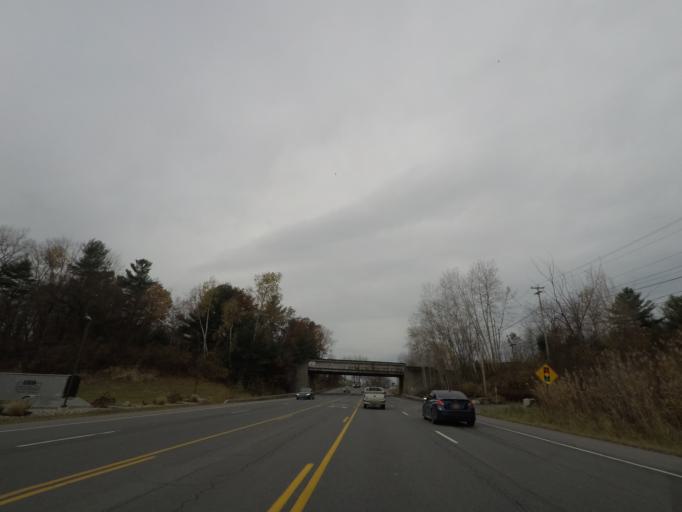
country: US
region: New York
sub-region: Saratoga County
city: Country Knolls
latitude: 42.9037
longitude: -73.7756
